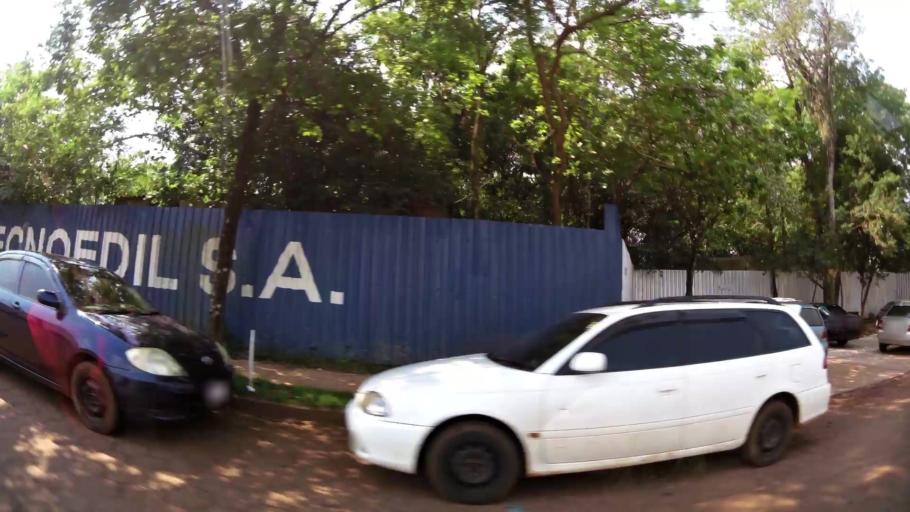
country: PY
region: Alto Parana
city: Ciudad del Este
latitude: -25.5134
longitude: -54.6249
